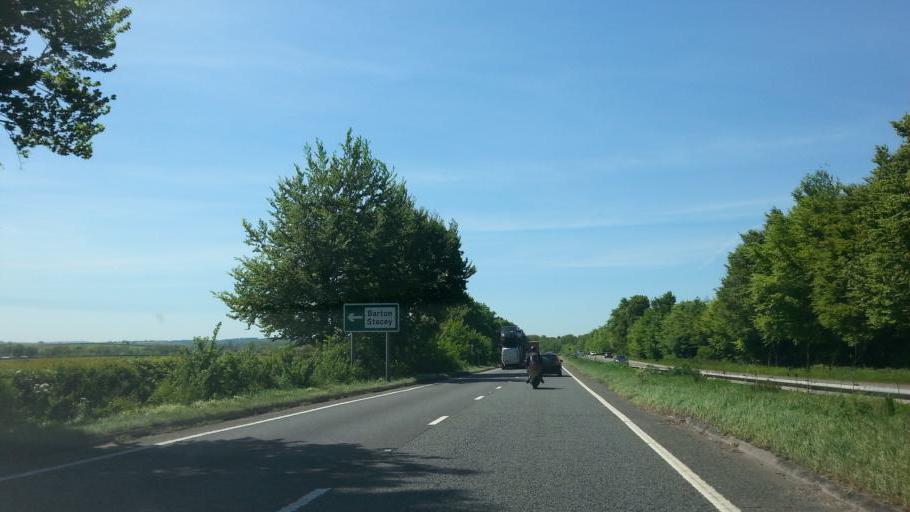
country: GB
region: England
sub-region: Hampshire
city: Kings Worthy
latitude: 51.1785
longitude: -1.3624
